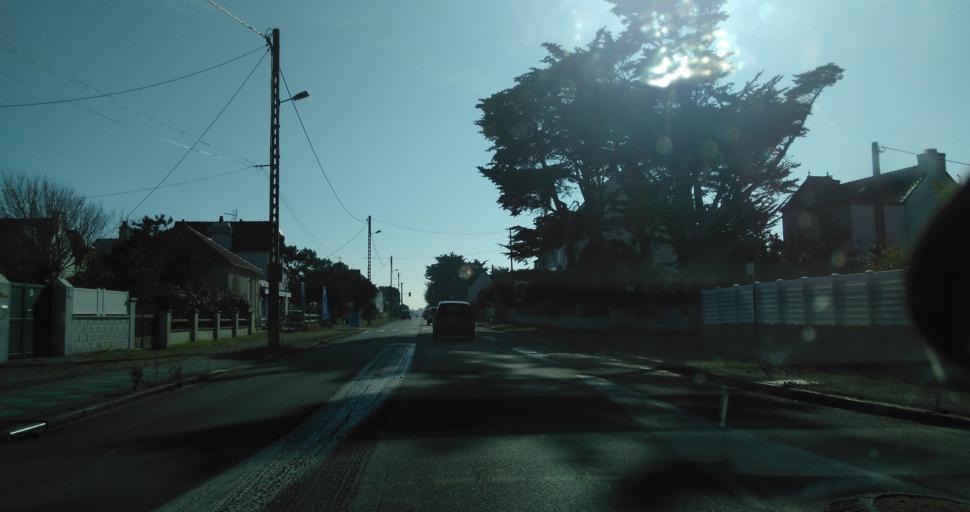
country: FR
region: Brittany
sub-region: Departement du Morbihan
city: Saint-Pierre-Quiberon
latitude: 47.5596
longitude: -3.1344
